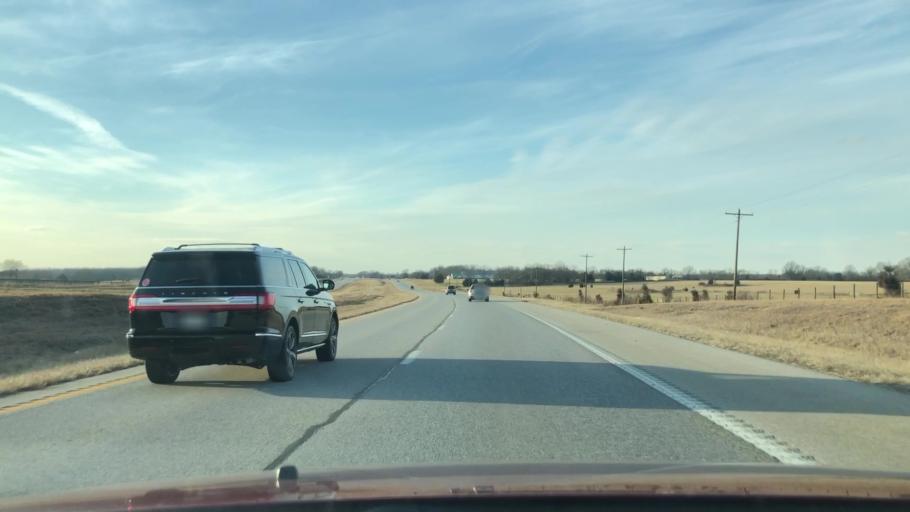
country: US
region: Missouri
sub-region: Webster County
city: Seymour
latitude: 37.1238
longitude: -92.7012
